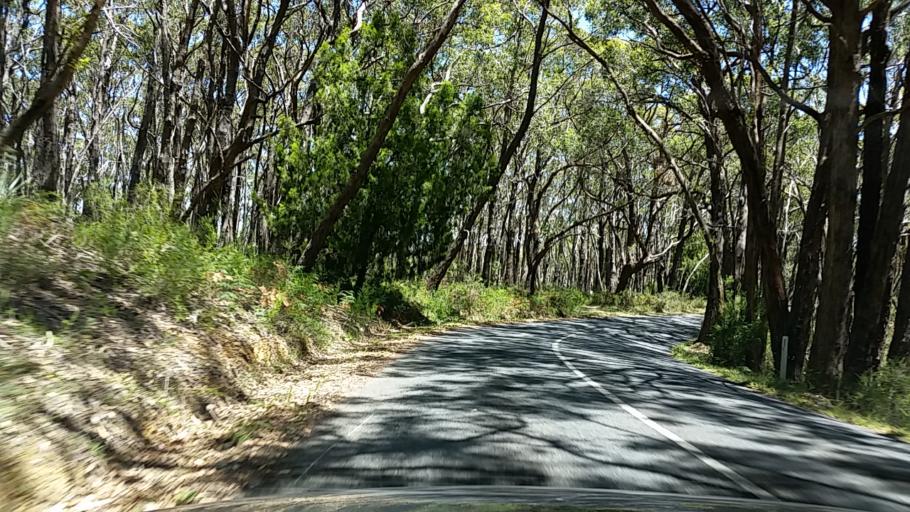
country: AU
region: South Australia
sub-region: Adelaide Hills
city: Crafers
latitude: -34.9933
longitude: 138.6932
